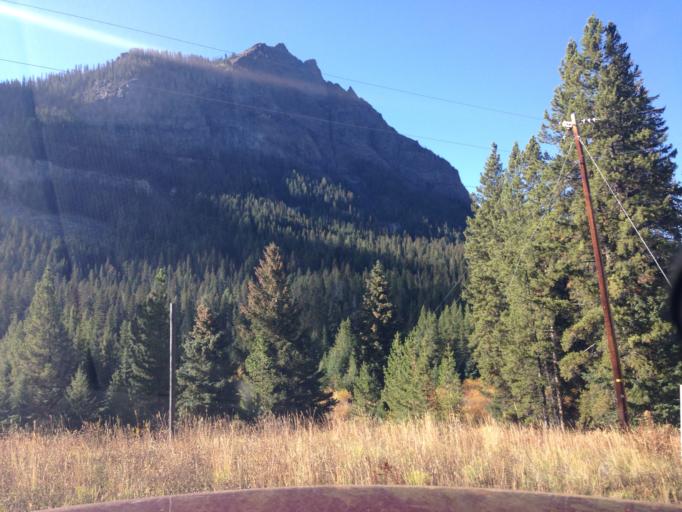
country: US
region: Montana
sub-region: Stillwater County
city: Absarokee
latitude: 45.0180
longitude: -109.9509
